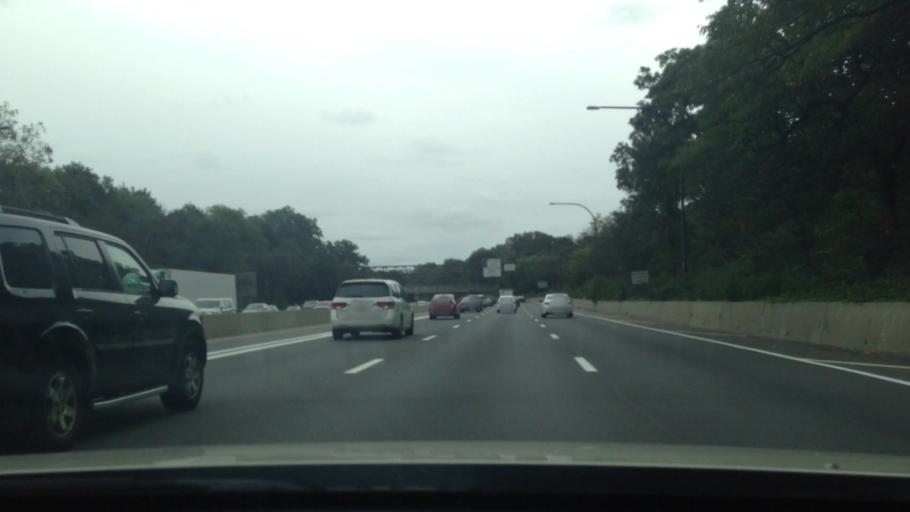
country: US
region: New York
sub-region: Nassau County
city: Old Westbury
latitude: 40.7817
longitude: -73.6118
